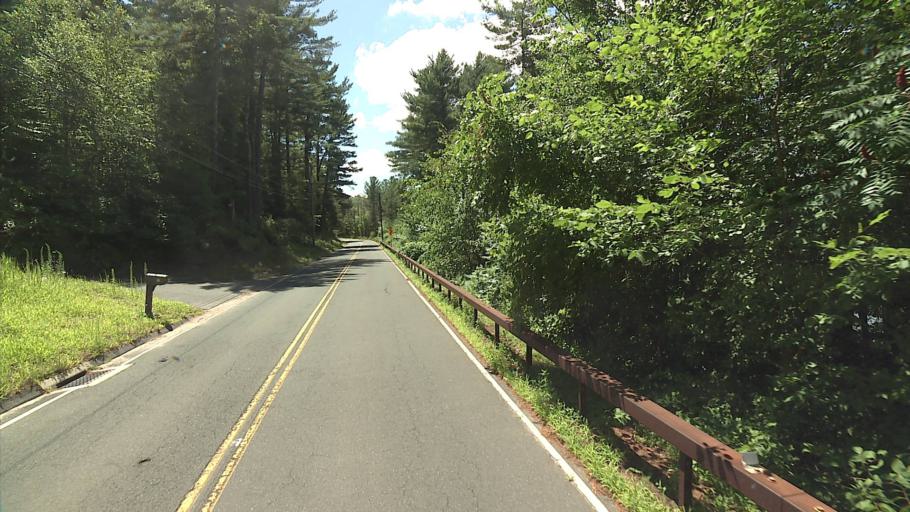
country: US
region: Connecticut
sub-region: Litchfield County
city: New Hartford Center
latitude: 41.8970
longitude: -72.9576
